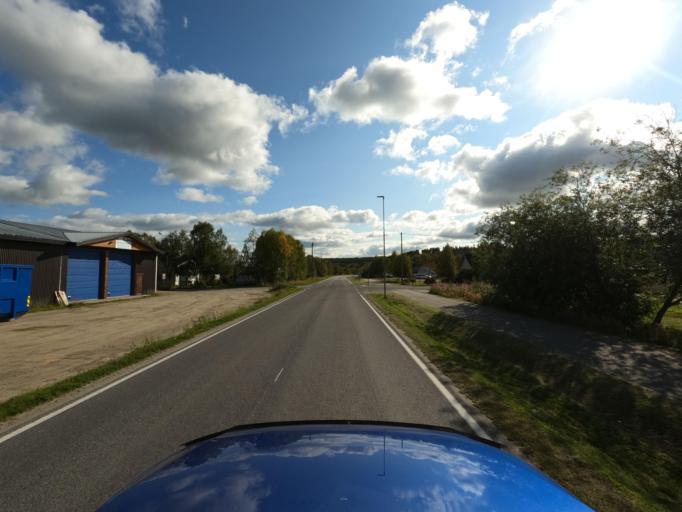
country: NO
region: Finnmark Fylke
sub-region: Karasjok
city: Karasjohka
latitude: 69.4644
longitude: 25.5078
